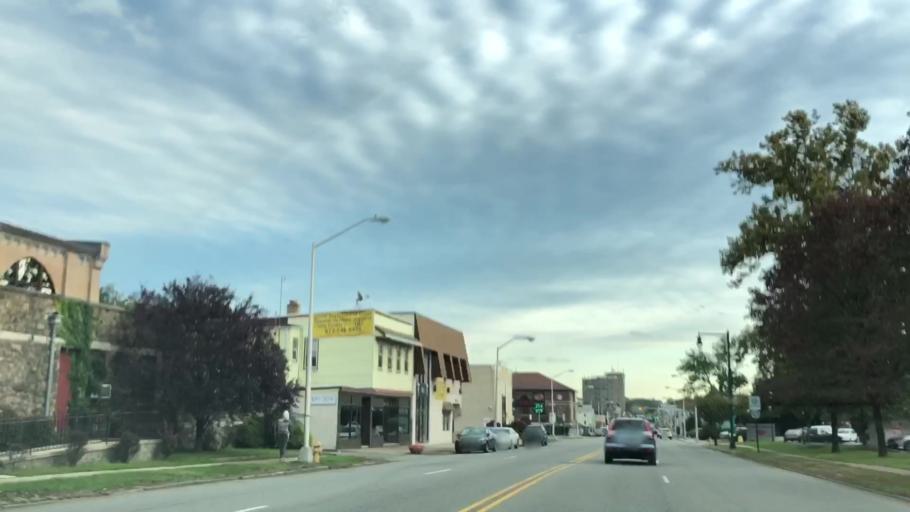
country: US
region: New Jersey
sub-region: Essex County
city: Glen Ridge
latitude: 40.7986
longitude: -74.2015
